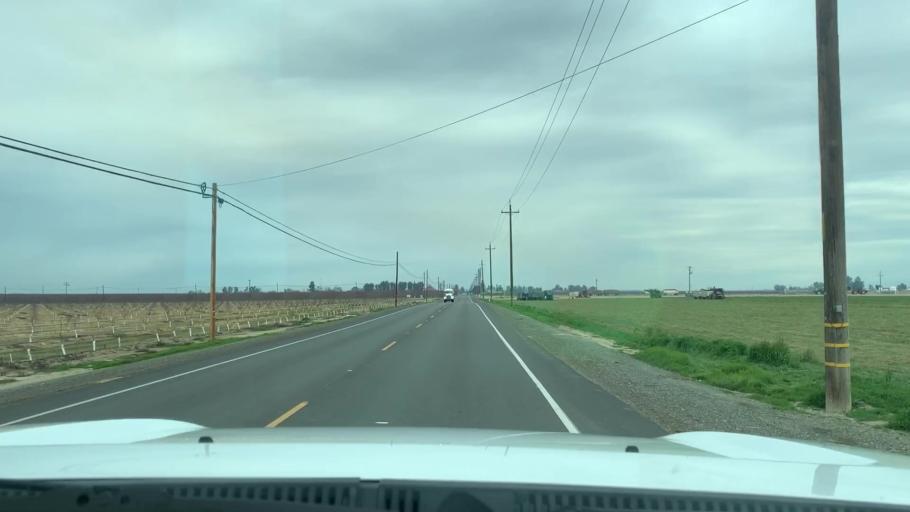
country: US
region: California
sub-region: Kern County
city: Shafter
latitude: 35.4092
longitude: -119.2519
